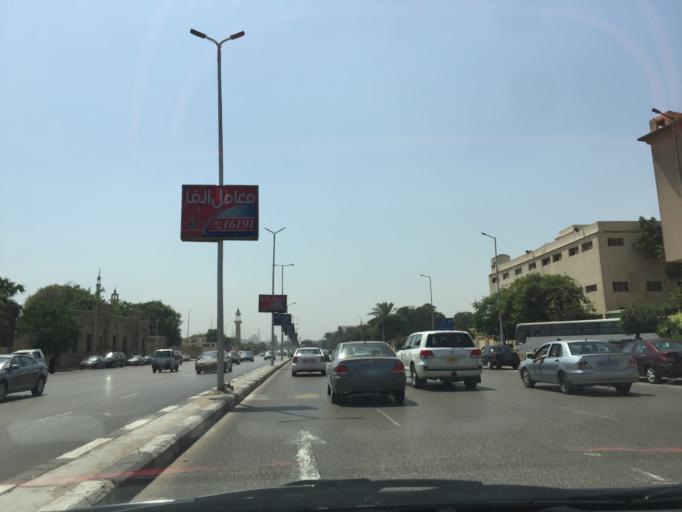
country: EG
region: Muhafazat al Qahirah
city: Cairo
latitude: 30.0519
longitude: 31.2766
